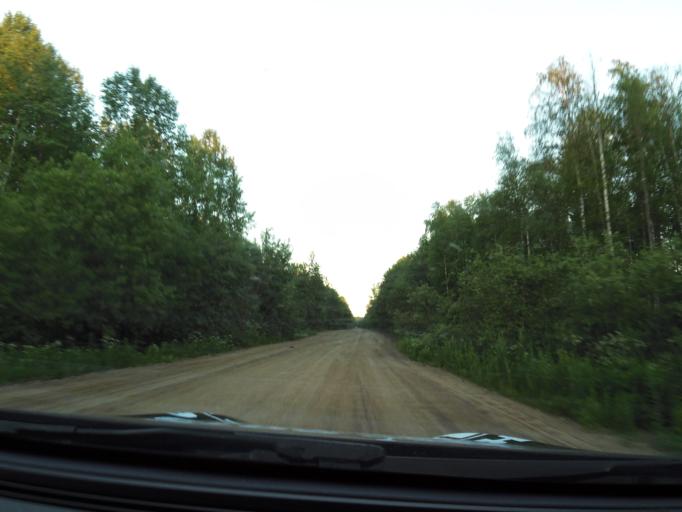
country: RU
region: Leningrad
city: Voznesen'ye
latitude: 60.9205
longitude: 35.4807
